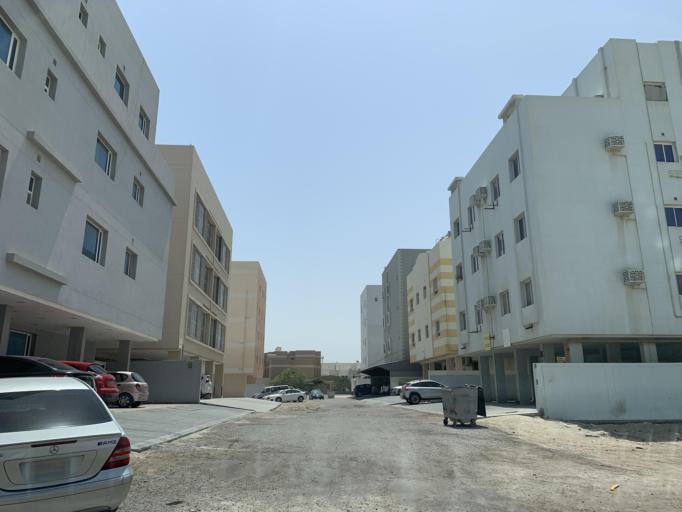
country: BH
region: Northern
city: Madinat `Isa
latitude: 26.1921
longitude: 50.5462
